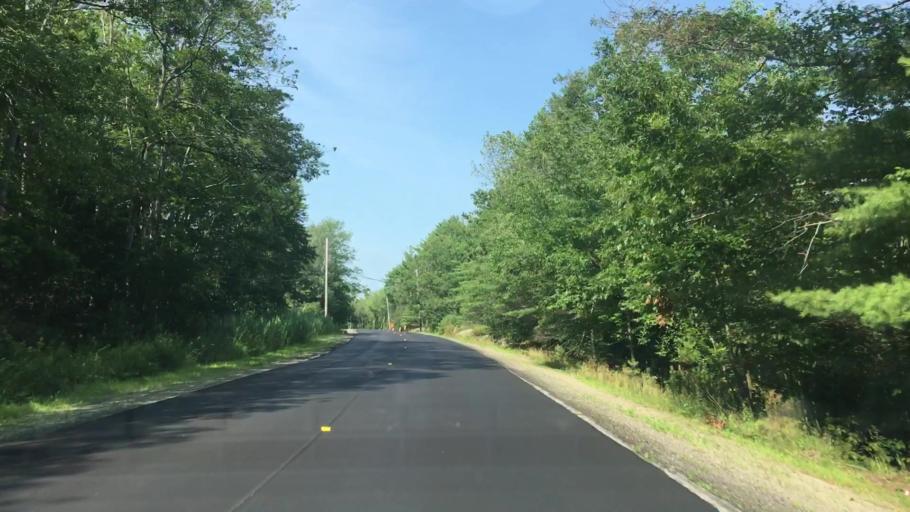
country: US
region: Maine
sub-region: Sagadahoc County
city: Woolwich
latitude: 43.9318
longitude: -69.8002
